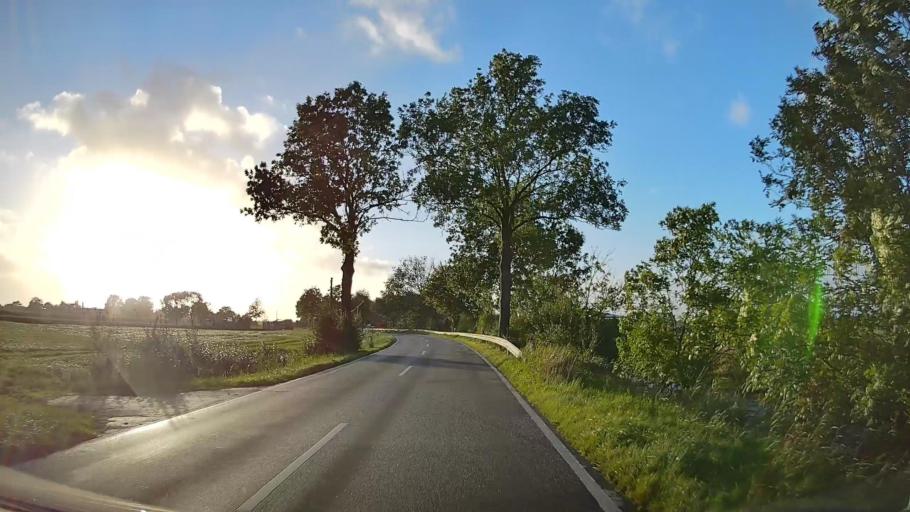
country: DE
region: Schleswig-Holstein
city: Herzhorn
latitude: 53.7945
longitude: 9.5024
